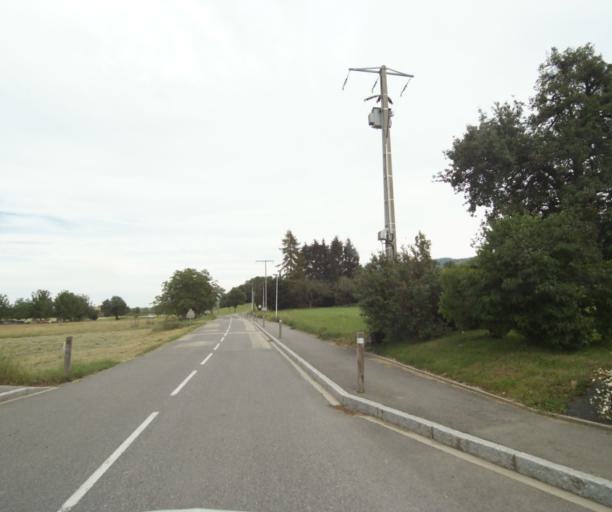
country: FR
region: Rhone-Alpes
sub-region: Departement de la Haute-Savoie
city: Bons-en-Chablais
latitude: 46.2682
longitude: 6.3966
